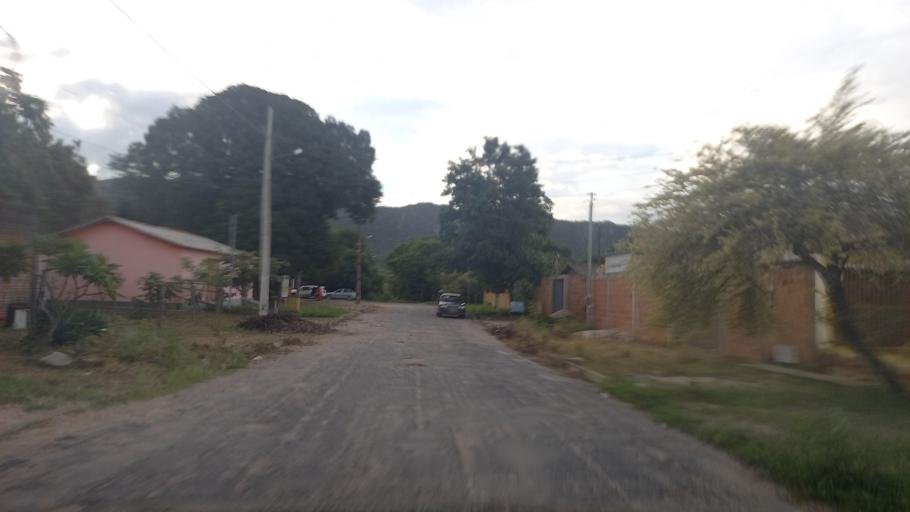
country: BR
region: Goias
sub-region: Cavalcante
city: Cavalcante
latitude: -13.7897
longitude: -47.4598
